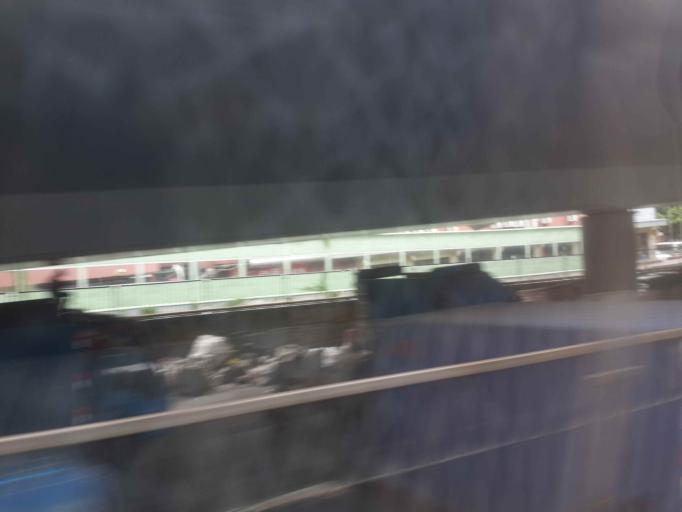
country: CN
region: Guangdong
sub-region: Shenzhen
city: Shenzhen
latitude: 22.5373
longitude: 114.1081
